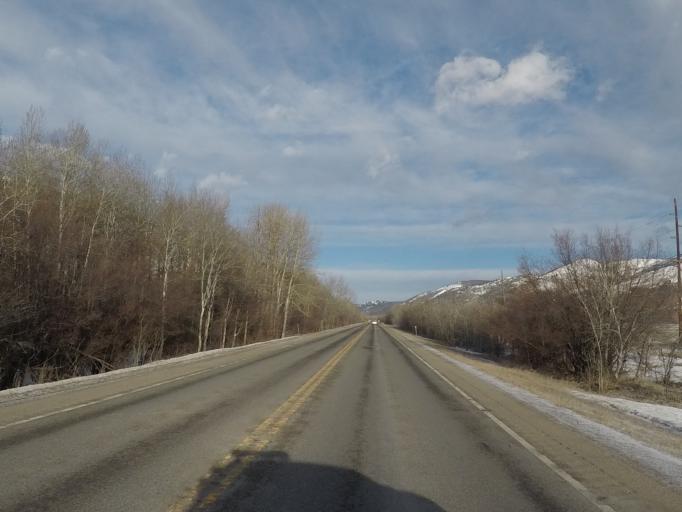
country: US
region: Montana
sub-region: Deer Lodge County
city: Anaconda
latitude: 46.1528
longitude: -113.0281
